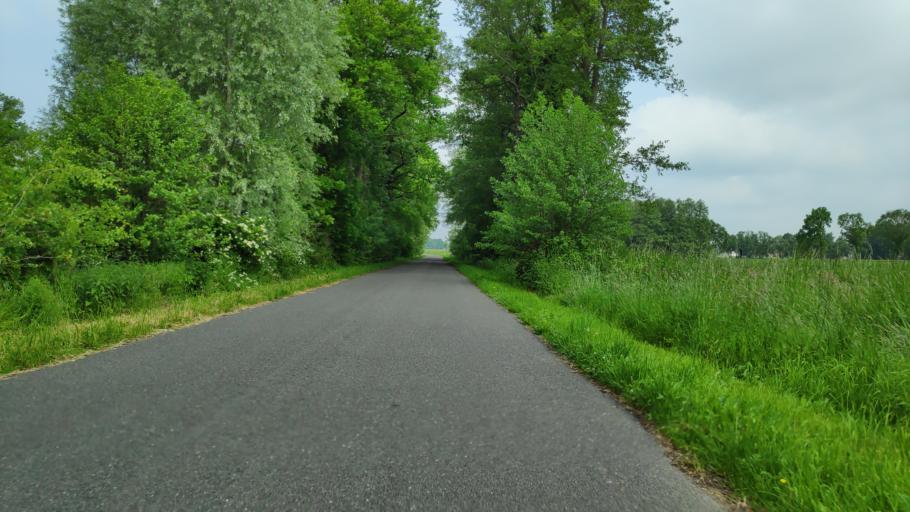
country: DE
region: North Rhine-Westphalia
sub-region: Regierungsbezirk Detmold
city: Hille
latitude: 52.3563
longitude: 8.7667
